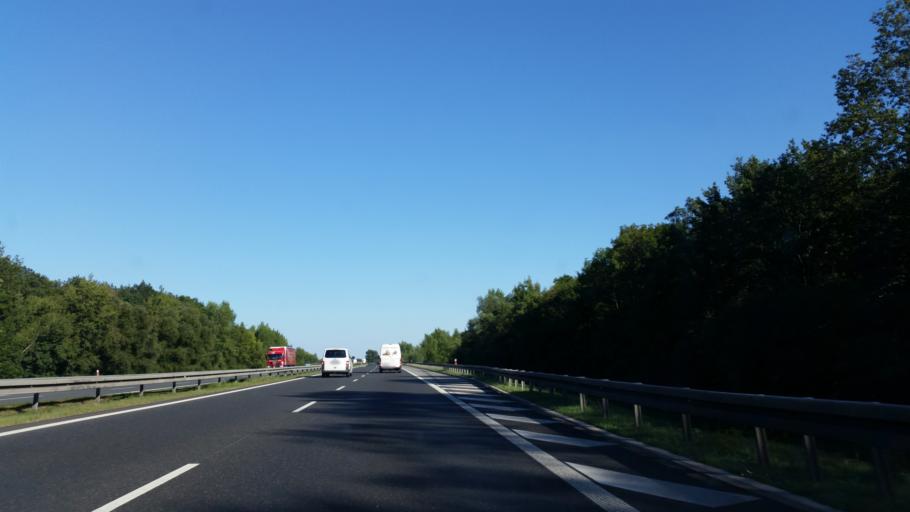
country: PL
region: Opole Voivodeship
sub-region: Powiat brzeski
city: Olszanka
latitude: 50.7286
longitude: 17.5107
